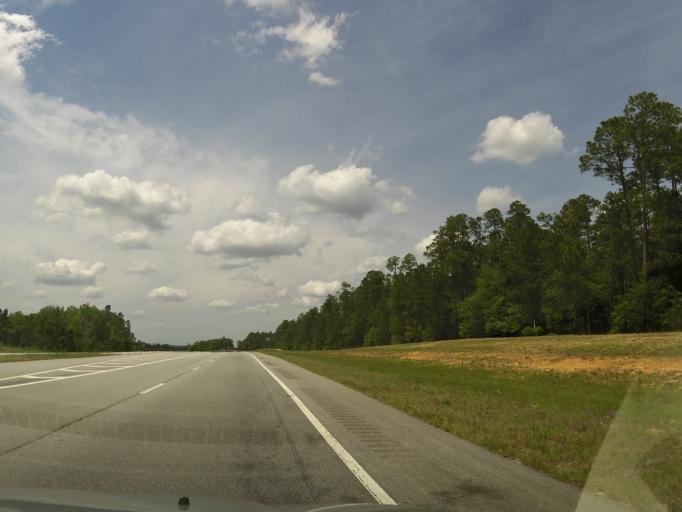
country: US
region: Georgia
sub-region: Emanuel County
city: Swainsboro
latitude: 32.6572
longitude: -82.3741
